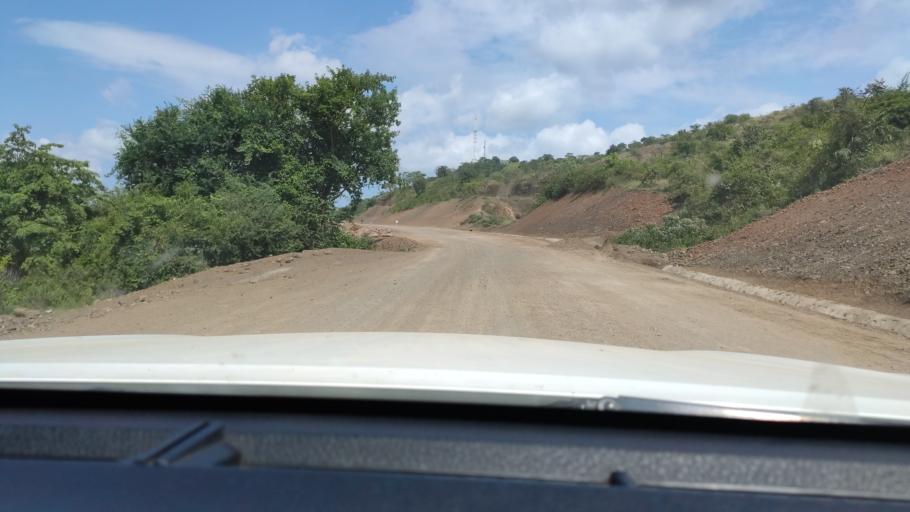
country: ET
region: Southern Nations, Nationalities, and People's Region
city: Felege Neway
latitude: 6.3909
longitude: 37.0670
